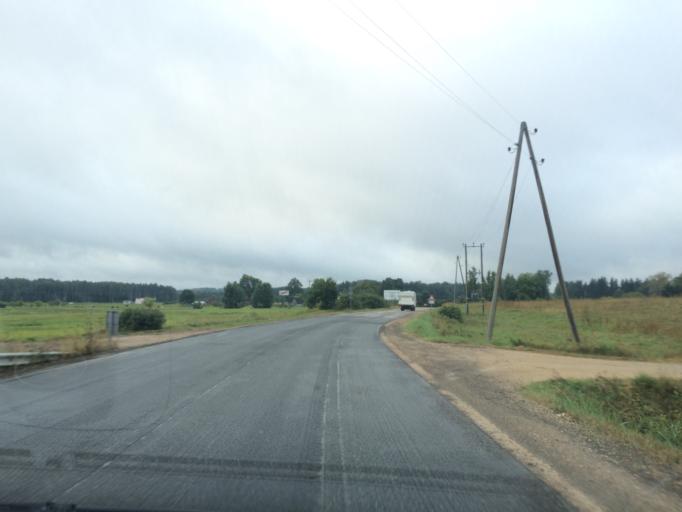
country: LV
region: Ikskile
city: Ikskile
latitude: 56.8637
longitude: 24.5595
